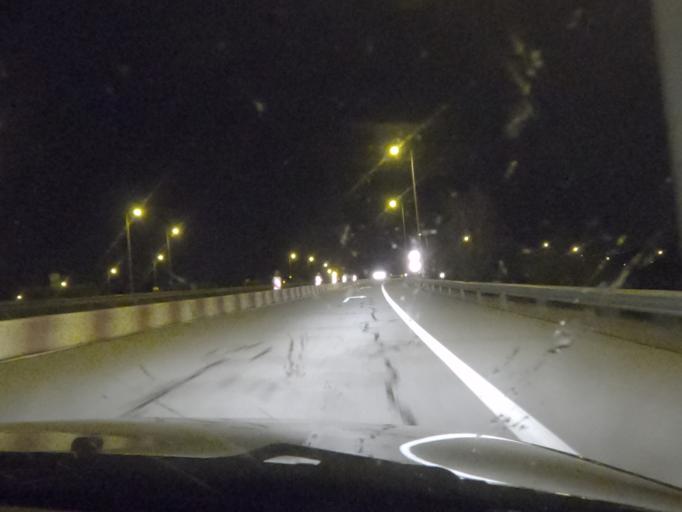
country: PT
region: Evora
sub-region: Estremoz
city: Estremoz
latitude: 38.8427
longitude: -7.6112
